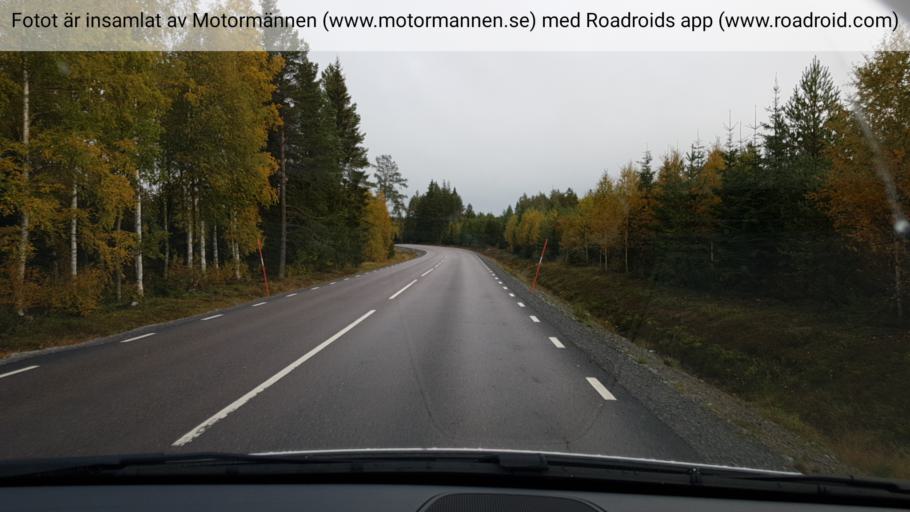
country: SE
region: Vaesterbotten
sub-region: Umea Kommun
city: Ersmark
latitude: 63.8991
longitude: 20.3148
